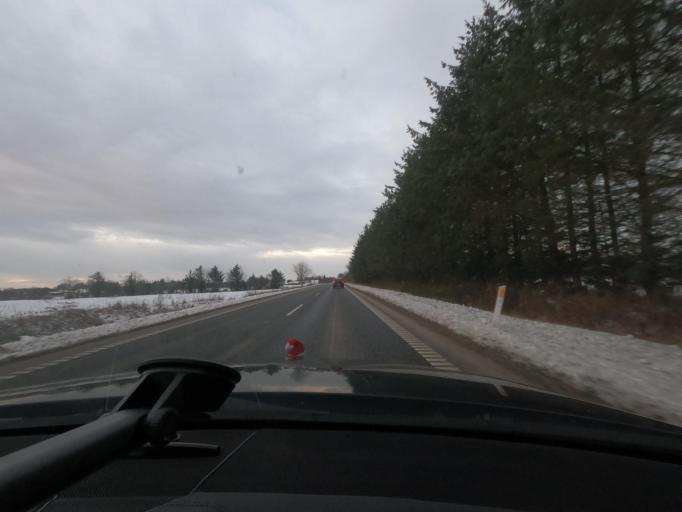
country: DK
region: South Denmark
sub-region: Aabenraa Kommune
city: Krusa
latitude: 54.8699
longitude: 9.4599
